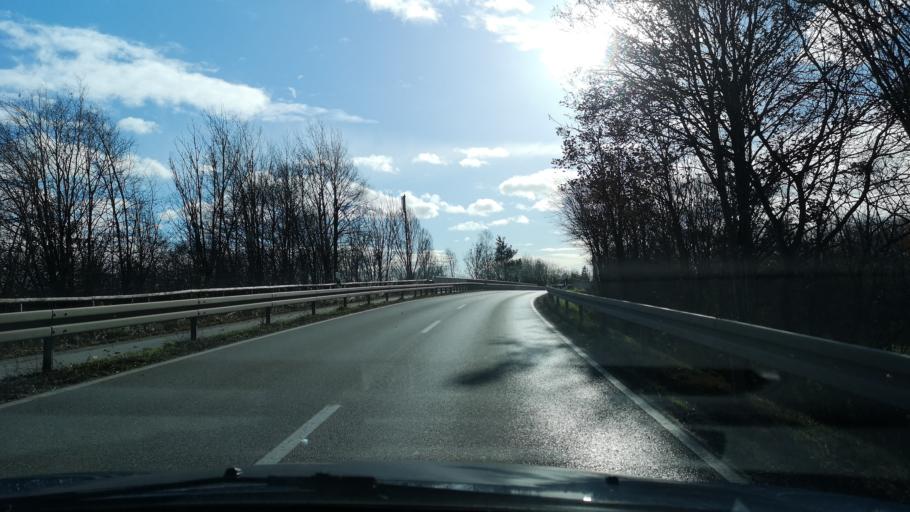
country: DE
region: Bavaria
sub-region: Upper Bavaria
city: Poing
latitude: 48.1555
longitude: 11.8179
